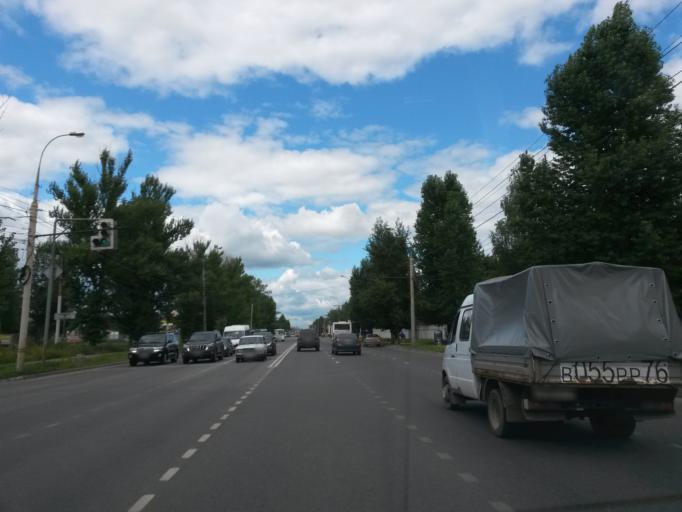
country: RU
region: Jaroslavl
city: Yaroslavl
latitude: 57.6568
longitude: 39.8445
